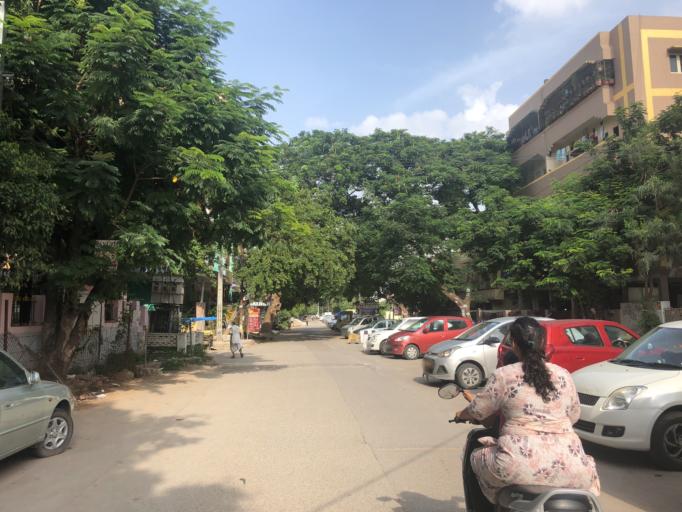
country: IN
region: Telangana
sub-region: Rangareddi
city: Kukatpalli
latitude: 17.4393
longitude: 78.4350
